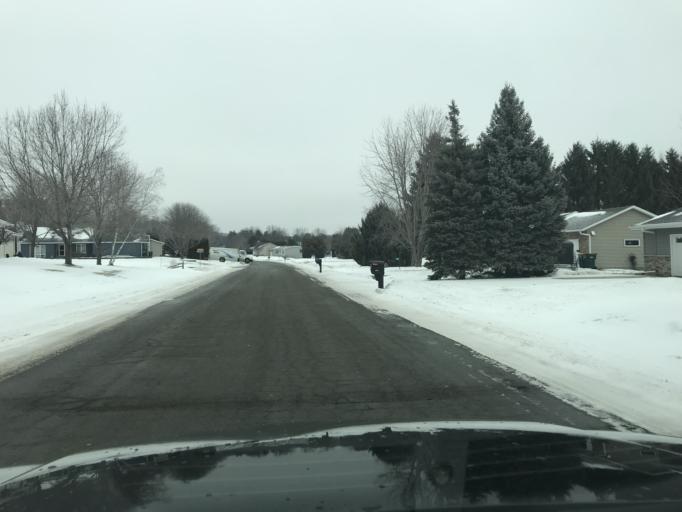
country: US
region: Wisconsin
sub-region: Dane County
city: Cottage Grove
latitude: 43.0943
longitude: -89.2161
